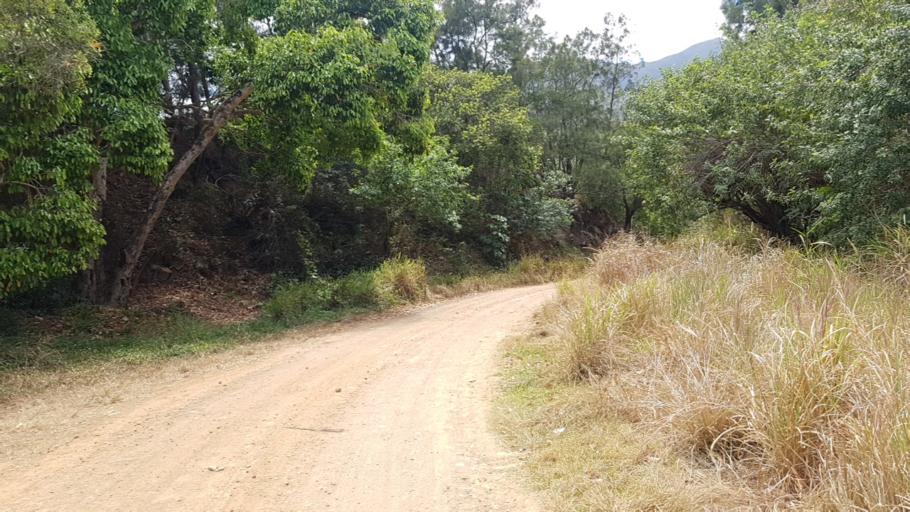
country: NC
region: South Province
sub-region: Dumbea
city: Dumbea
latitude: -22.1806
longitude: 166.4809
